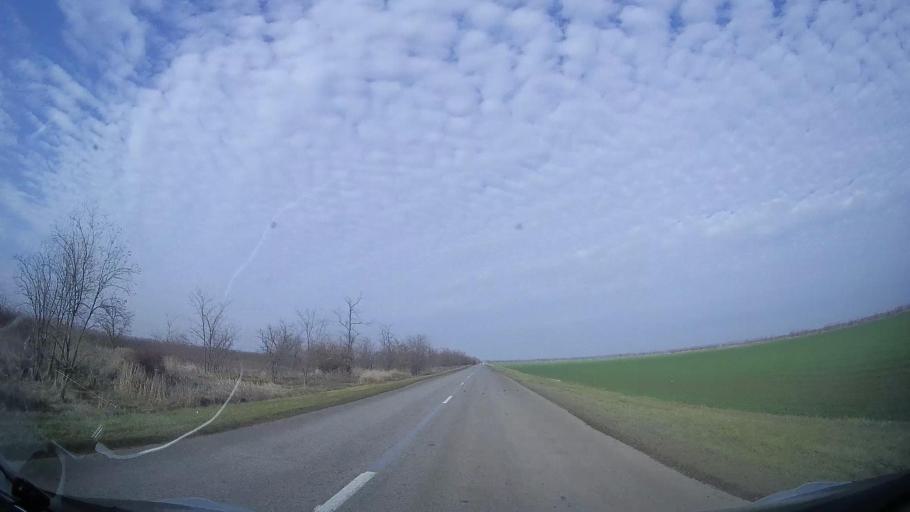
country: RU
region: Rostov
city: Gigant
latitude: 46.8613
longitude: 41.2794
